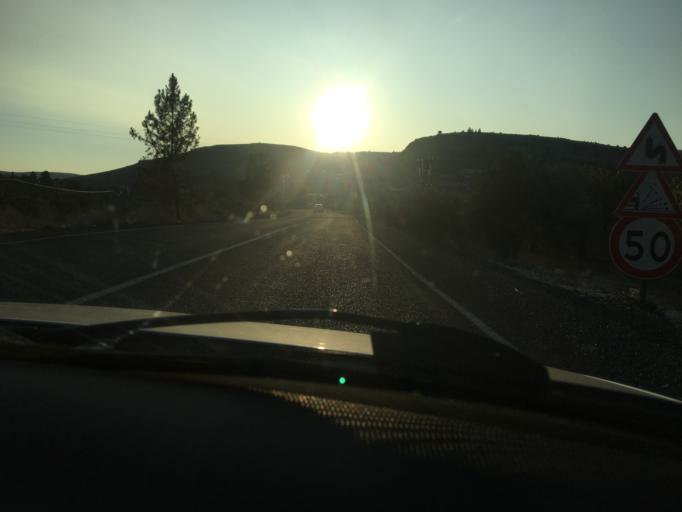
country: TR
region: Sanliurfa
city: Halfeti
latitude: 37.2221
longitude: 37.9571
